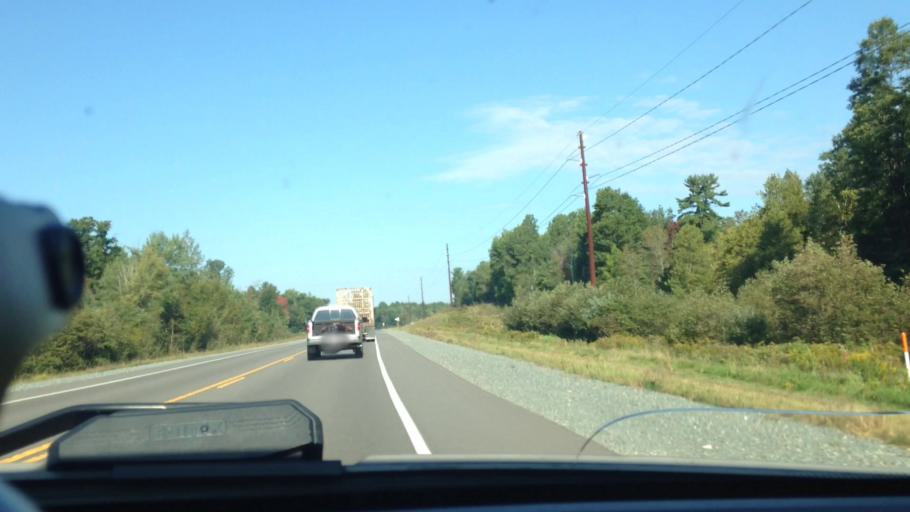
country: US
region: Michigan
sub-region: Dickinson County
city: Iron Mountain
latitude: 45.8772
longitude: -88.1183
